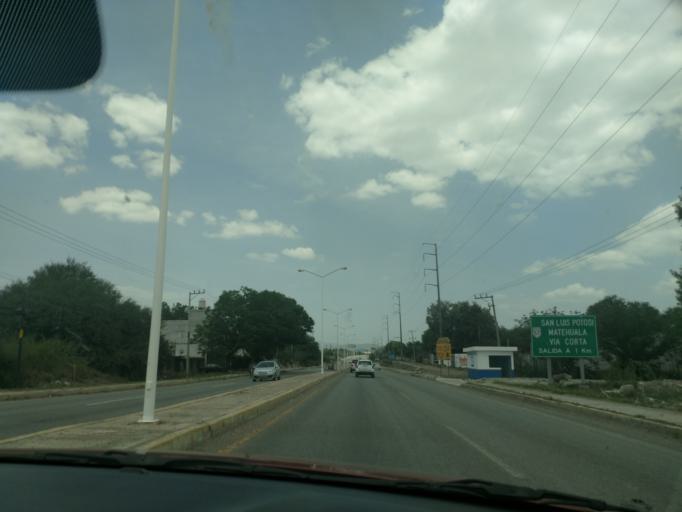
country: MX
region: San Luis Potosi
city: Rio Verde
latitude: 21.9219
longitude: -99.9698
